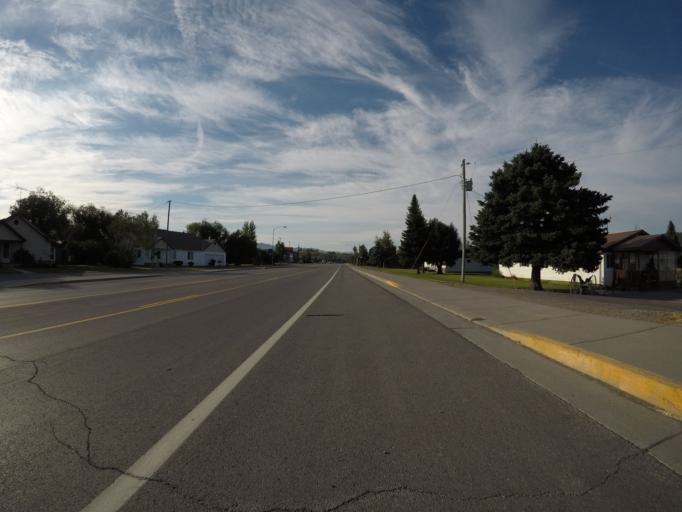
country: US
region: Wyoming
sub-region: Lincoln County
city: Afton
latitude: 42.9165
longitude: -111.0021
